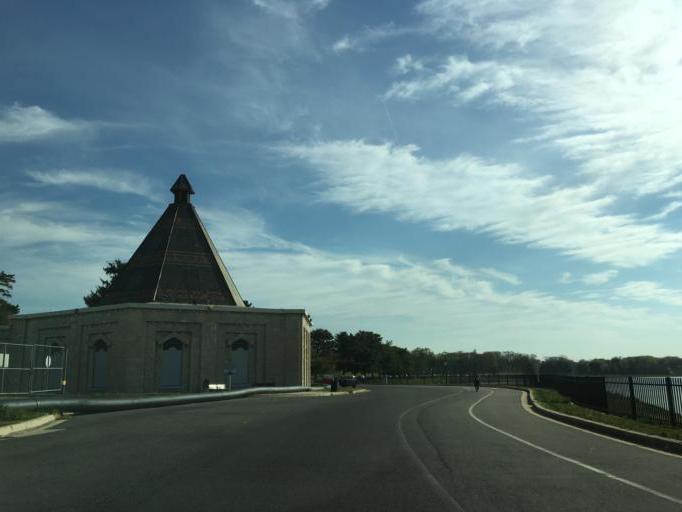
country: US
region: Maryland
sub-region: City of Baltimore
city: Baltimore
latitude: 39.3317
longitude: -76.5875
